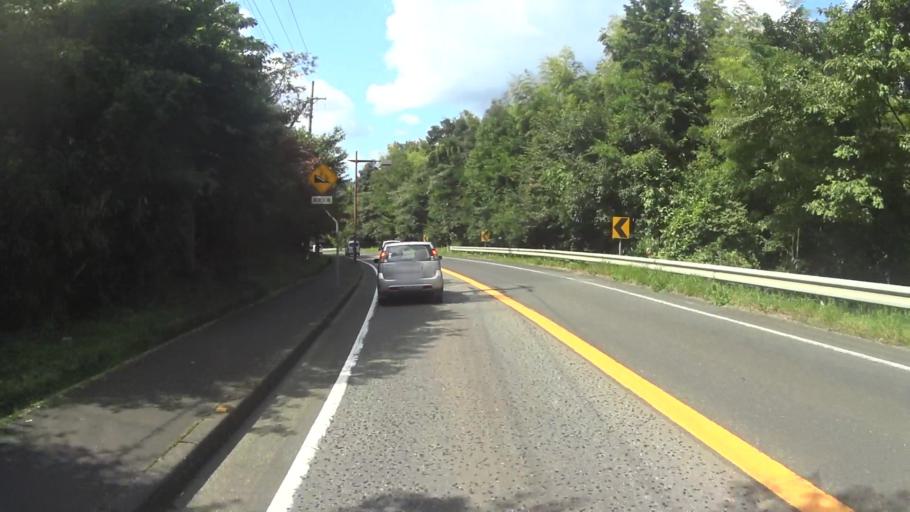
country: JP
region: Kyoto
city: Miyazu
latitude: 35.5517
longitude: 135.1659
